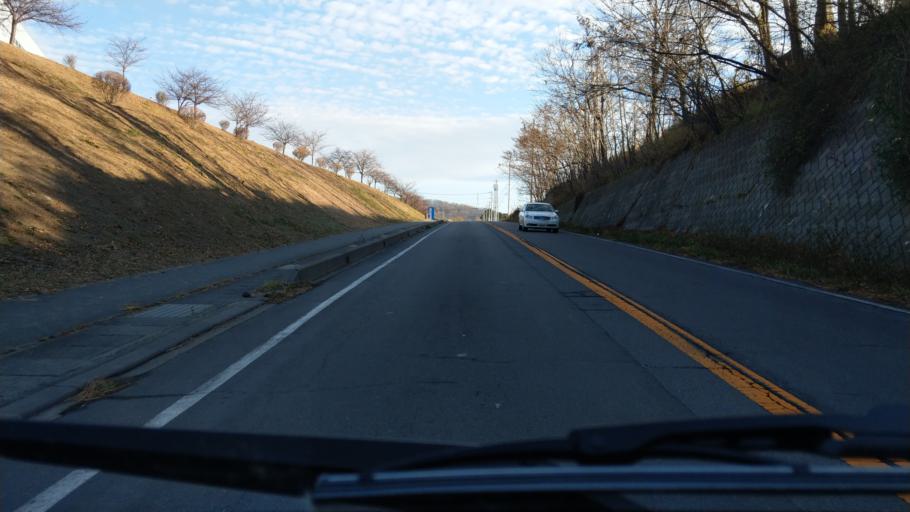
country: JP
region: Nagano
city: Ueda
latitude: 36.3974
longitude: 138.2953
